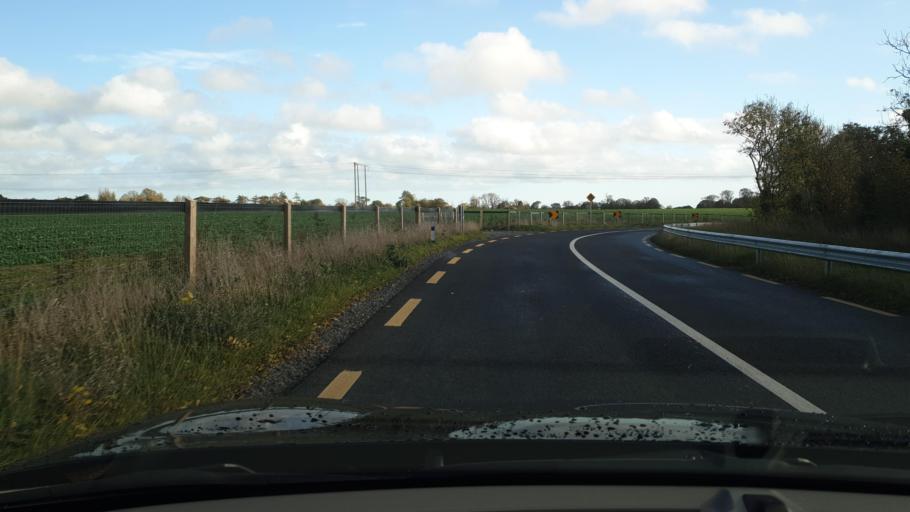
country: IE
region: Leinster
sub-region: An Mhi
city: Ashbourne
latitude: 53.4969
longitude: -6.3800
